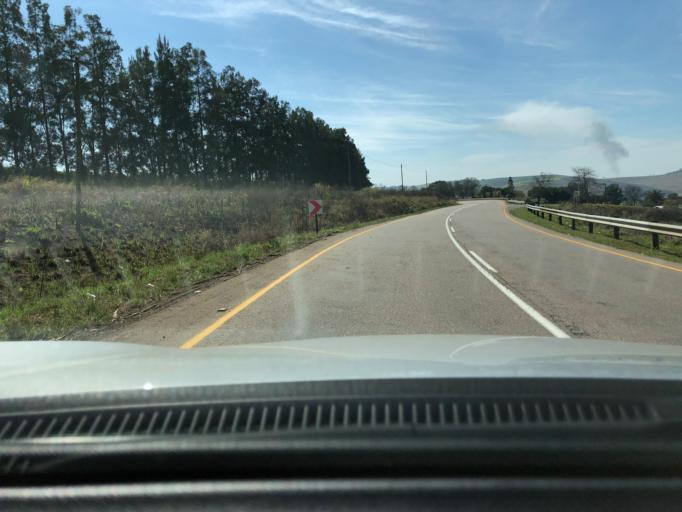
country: ZA
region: KwaZulu-Natal
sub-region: uMgungundlovu District Municipality
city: Richmond
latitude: -29.7882
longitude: 30.3503
